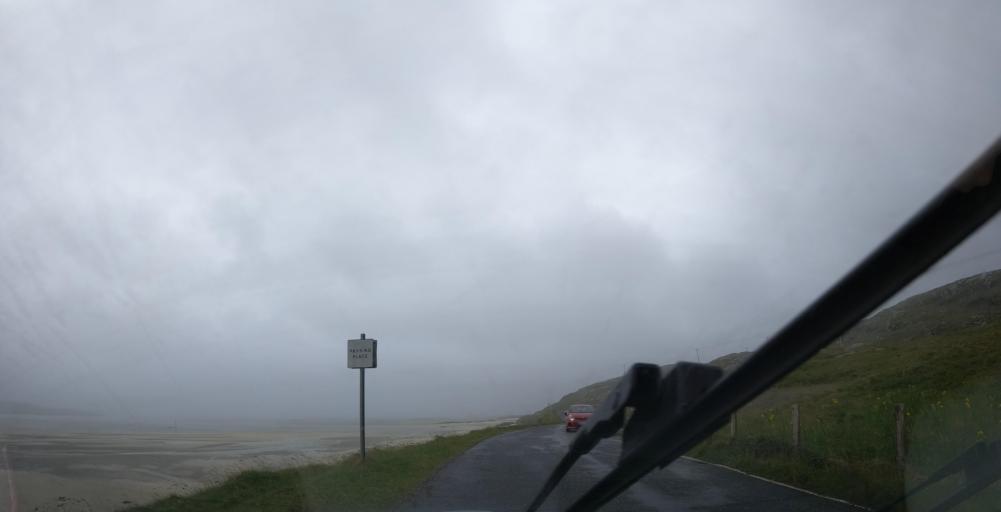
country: GB
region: Scotland
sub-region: Eilean Siar
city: Barra
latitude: 57.0189
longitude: -7.4422
